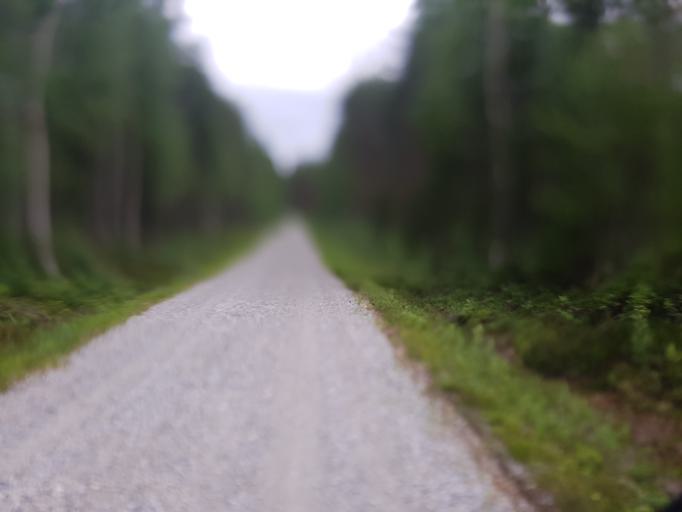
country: FI
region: Kainuu
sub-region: Kehys-Kainuu
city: Kuhmo
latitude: 64.4527
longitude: 29.7149
